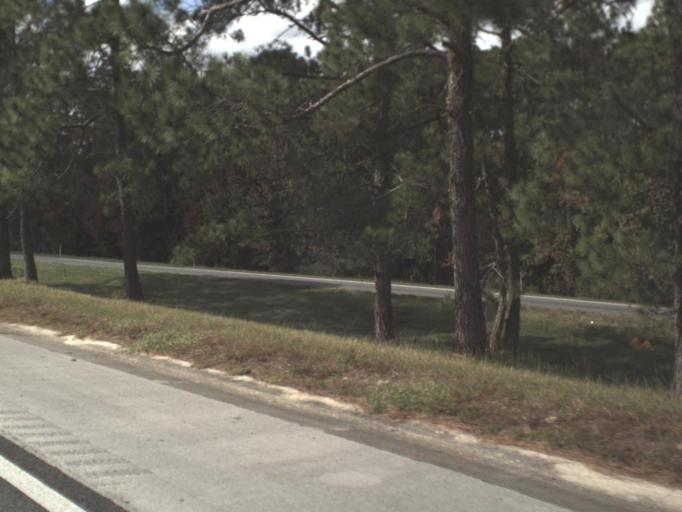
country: US
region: Florida
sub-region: Orange County
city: Christmas
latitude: 28.4527
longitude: -80.9812
